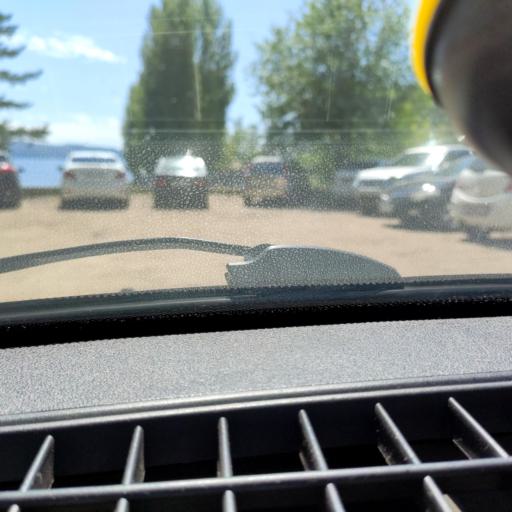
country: RU
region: Samara
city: Tol'yatti
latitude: 53.4739
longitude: 49.3339
